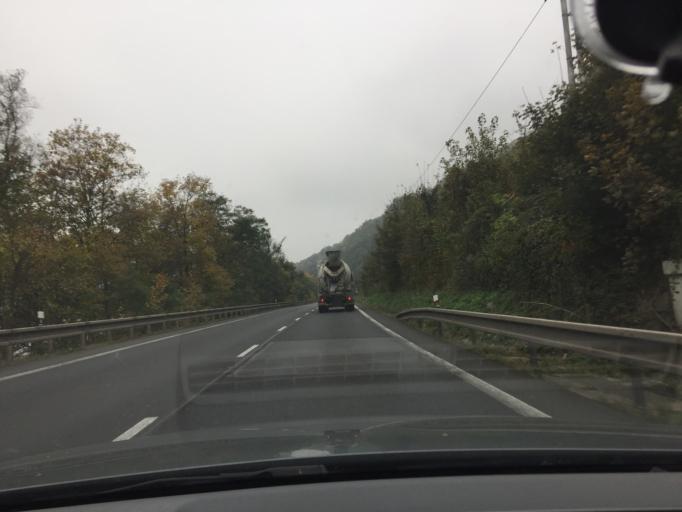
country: CZ
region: Ustecky
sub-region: Okres Usti nad Labem
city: Usti nad Labem
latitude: 50.6090
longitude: 14.0735
